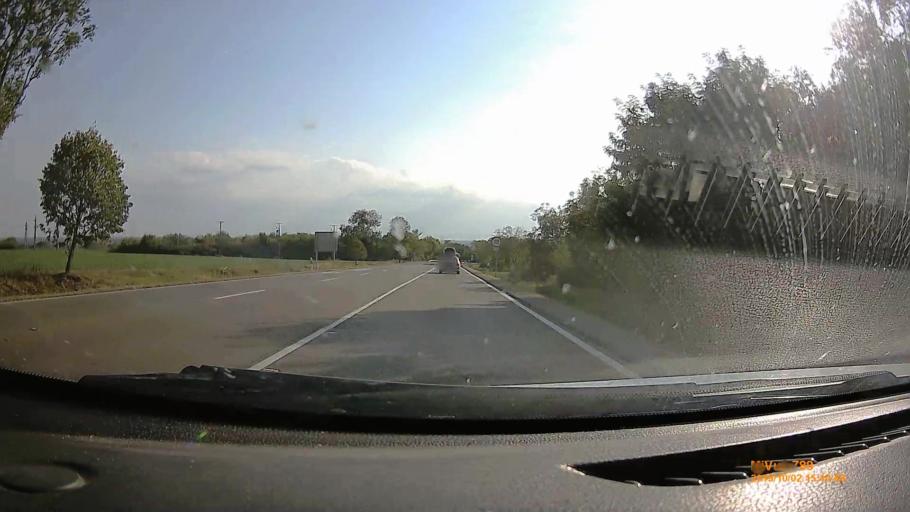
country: HU
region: Heves
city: Kerecsend
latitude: 47.8016
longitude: 20.3559
